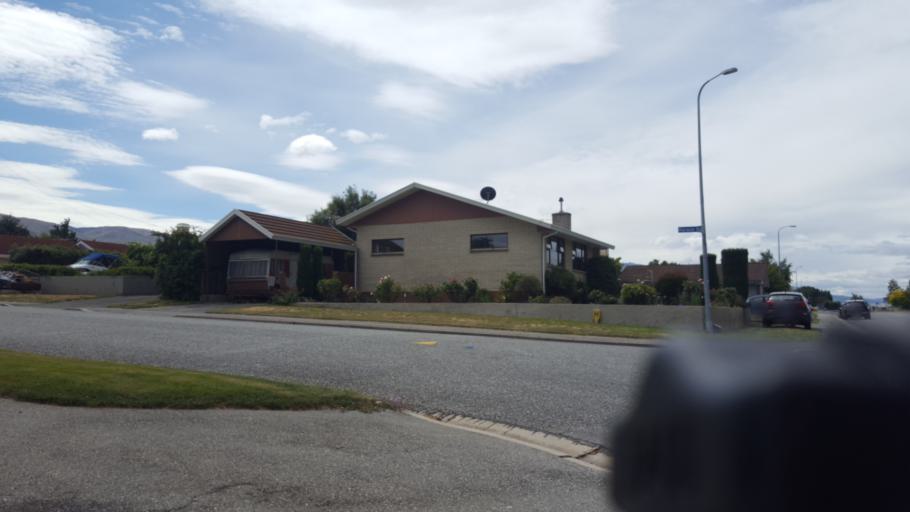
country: NZ
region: Otago
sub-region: Queenstown-Lakes District
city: Wanaka
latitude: -45.0451
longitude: 169.2129
